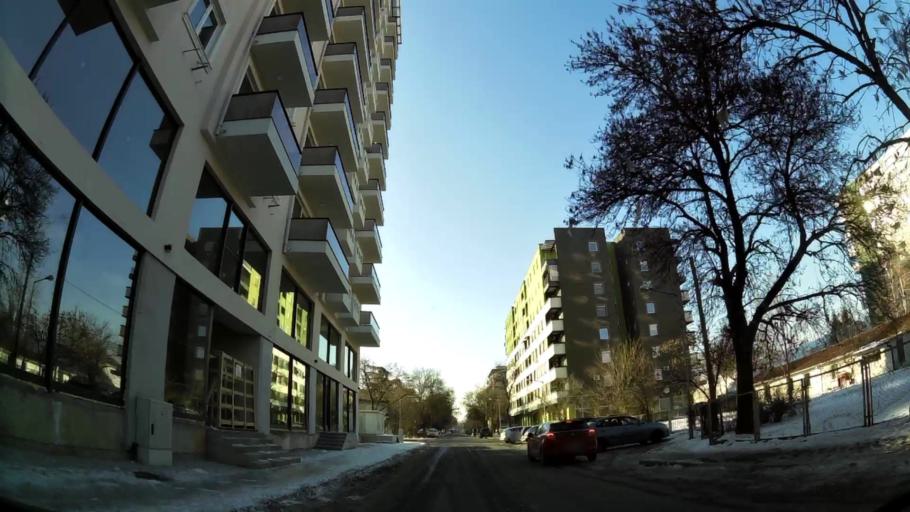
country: MK
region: Karpos
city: Skopje
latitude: 41.9999
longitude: 21.4037
